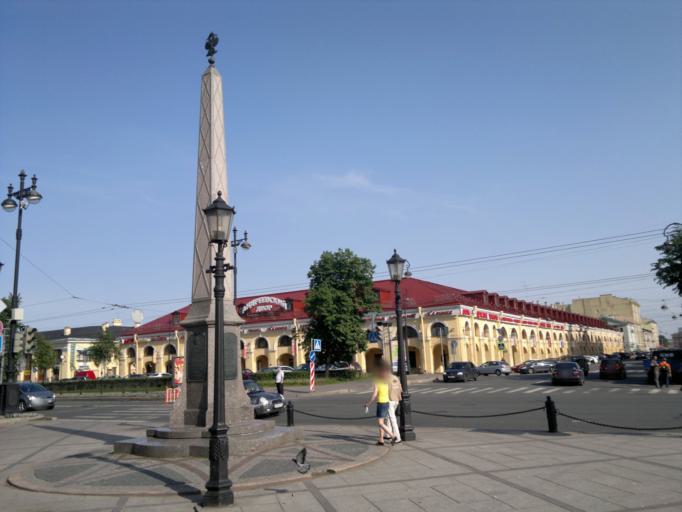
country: RU
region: St.-Petersburg
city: Vasyl'evsky Ostrov
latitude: 59.9393
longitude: 30.2828
